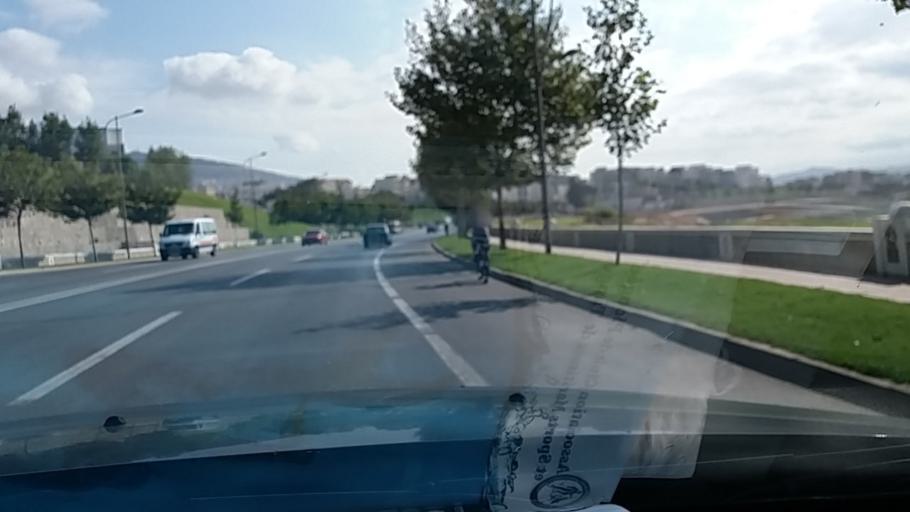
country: MA
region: Tanger-Tetouan
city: Tetouan
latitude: 35.5667
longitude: -5.4088
